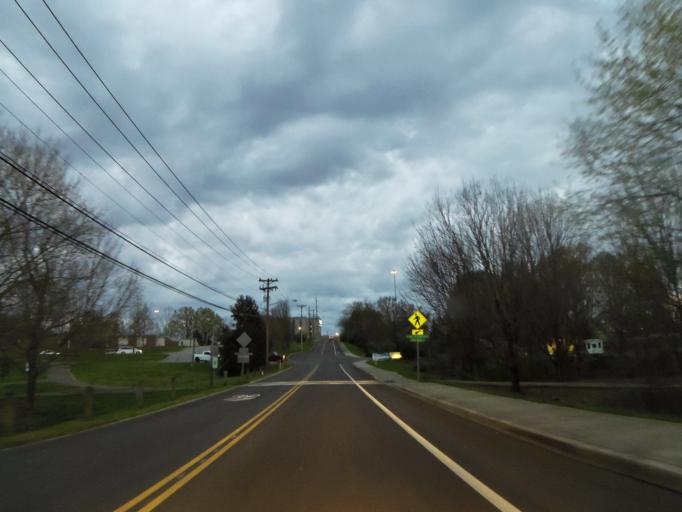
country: US
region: Tennessee
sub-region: Blount County
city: Louisville
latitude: 35.9304
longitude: -84.0474
